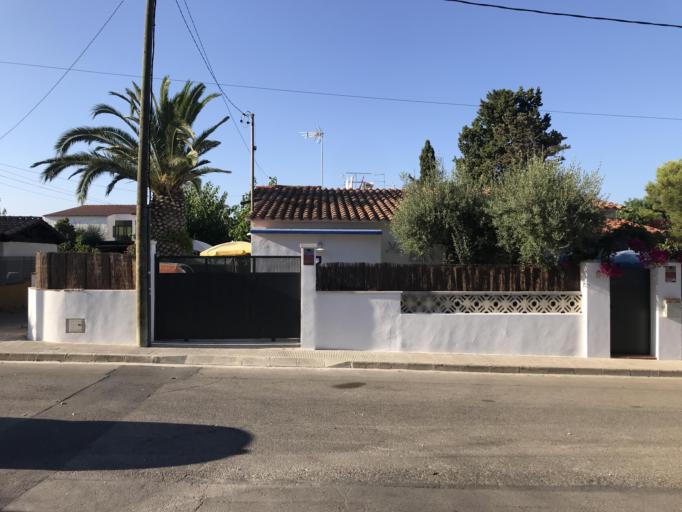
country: ES
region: Catalonia
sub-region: Provincia de Tarragona
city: Torredembarra
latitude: 41.1373
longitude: 1.3976
